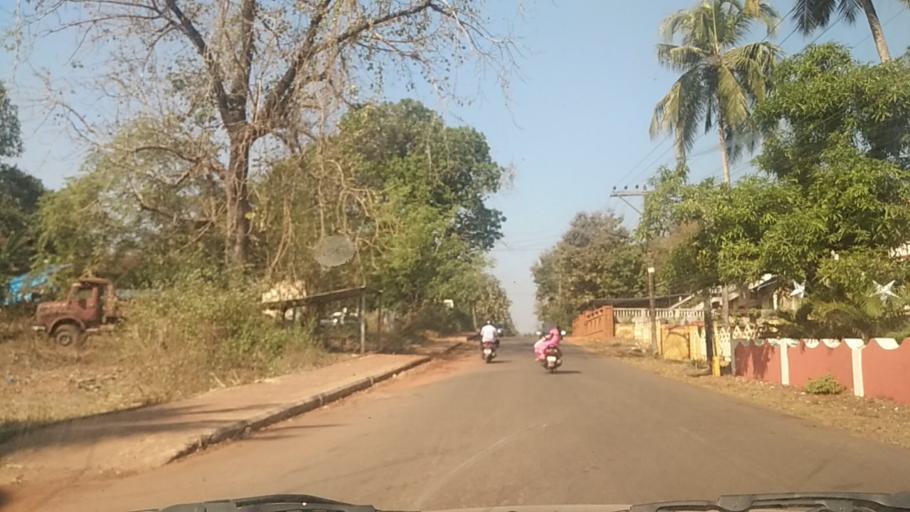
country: IN
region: Goa
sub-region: South Goa
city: Sanguem
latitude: 15.2270
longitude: 74.1567
